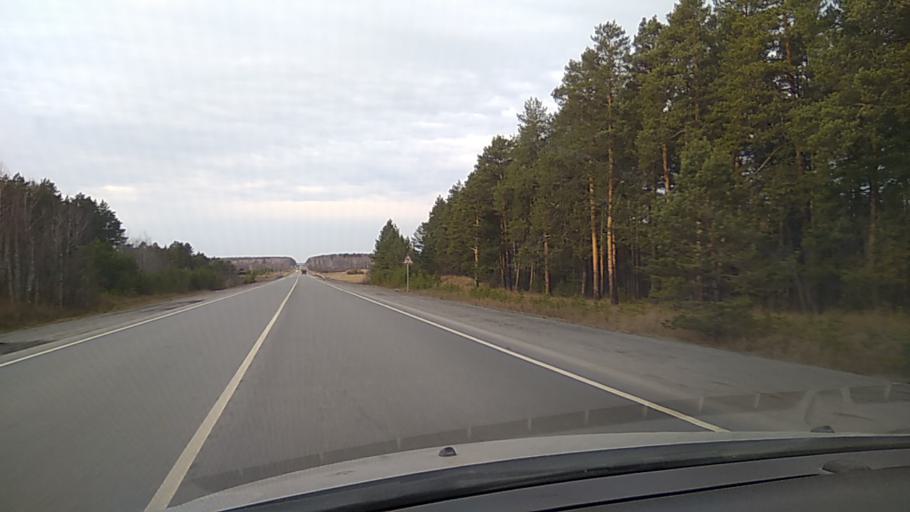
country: RU
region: Sverdlovsk
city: Troitskiy
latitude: 57.0889
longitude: 63.8693
